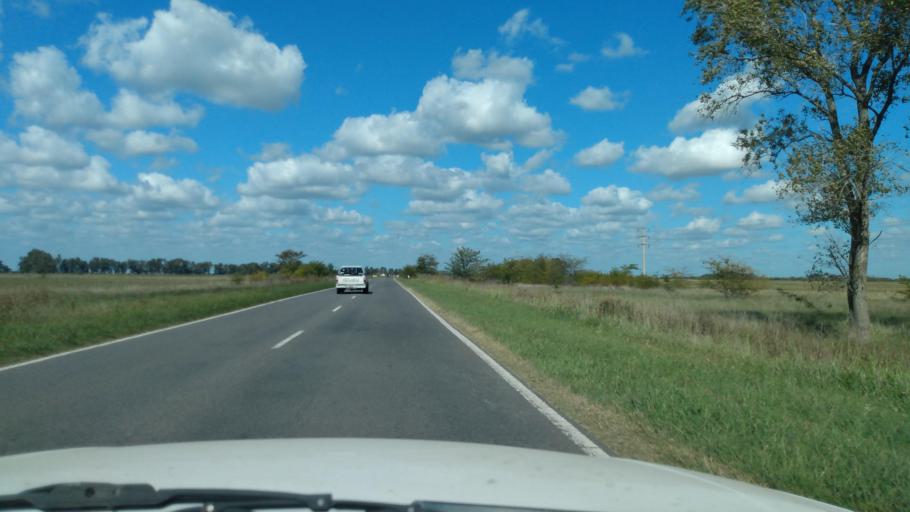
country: AR
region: Buenos Aires
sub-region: Partido de Navarro
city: Navarro
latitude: -34.8713
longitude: -59.3420
